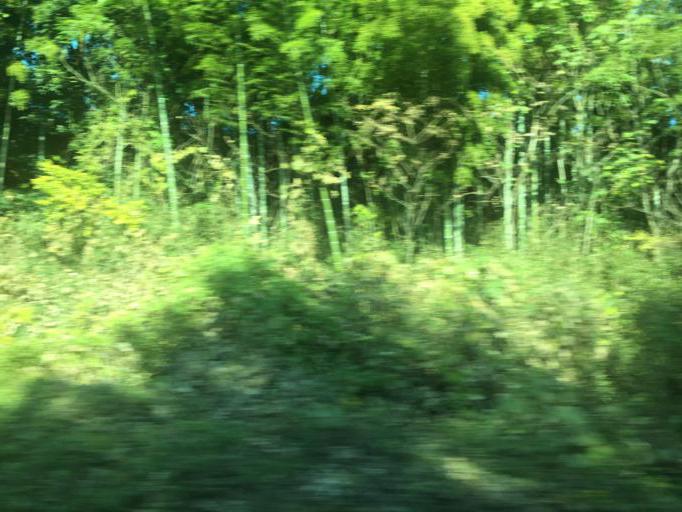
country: JP
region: Ibaraki
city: Kasama
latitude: 36.3655
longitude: 140.2578
